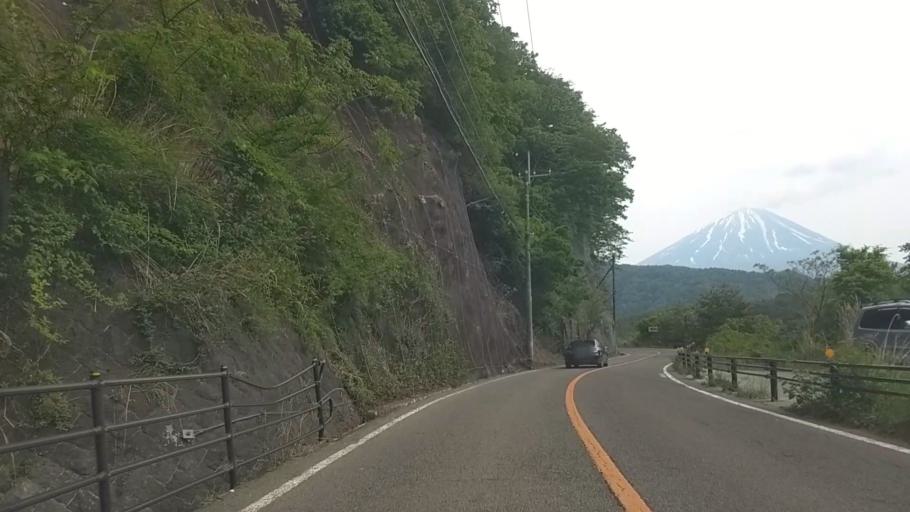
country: JP
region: Yamanashi
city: Fujikawaguchiko
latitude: 35.5002
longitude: 138.6661
